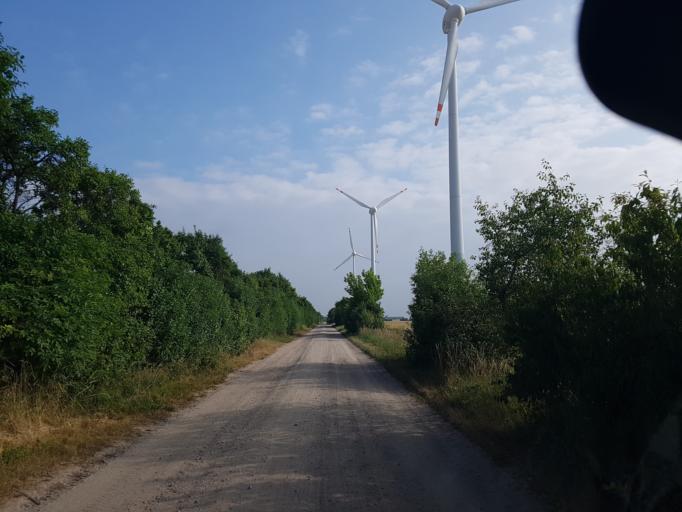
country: DE
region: Saxony-Anhalt
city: Kropstadt
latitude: 51.9968
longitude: 12.8181
